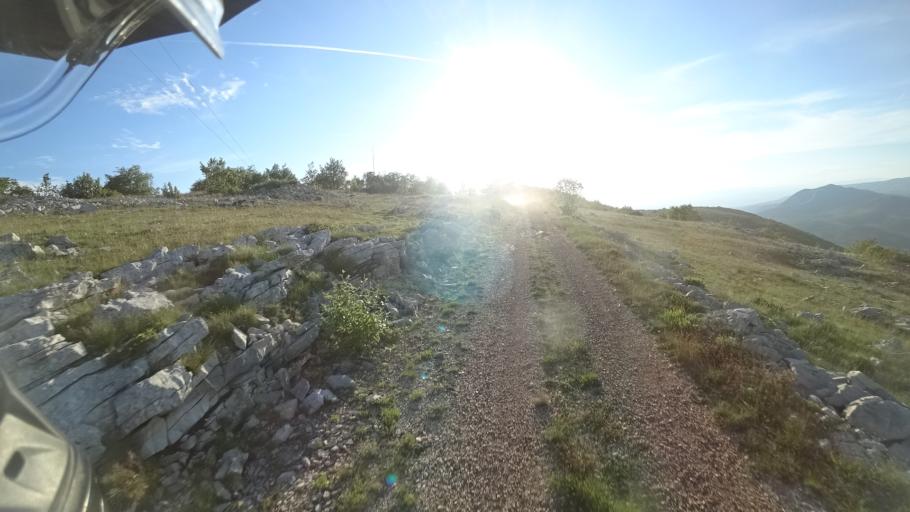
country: HR
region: Sibensko-Kniniska
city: Drnis
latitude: 43.8710
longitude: 16.3767
